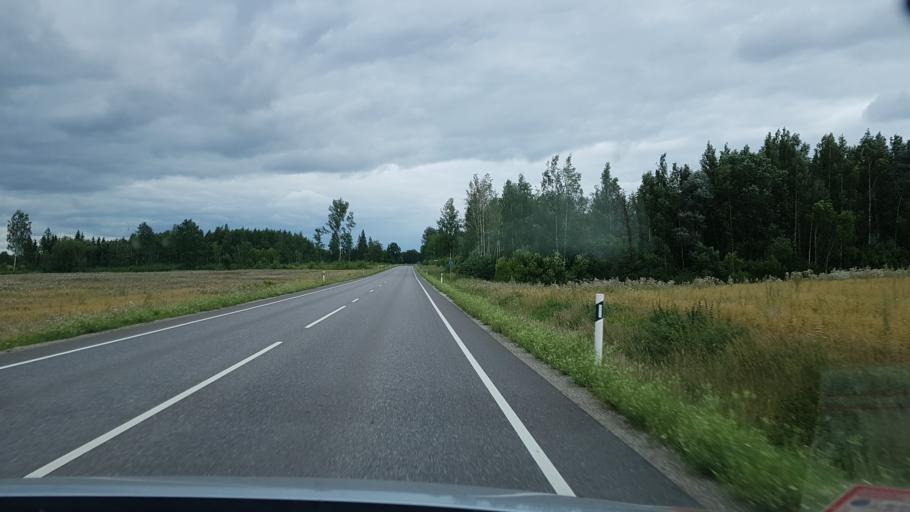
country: EE
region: Tartu
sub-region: Tartu linn
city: Tartu
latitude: 58.4412
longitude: 26.8201
